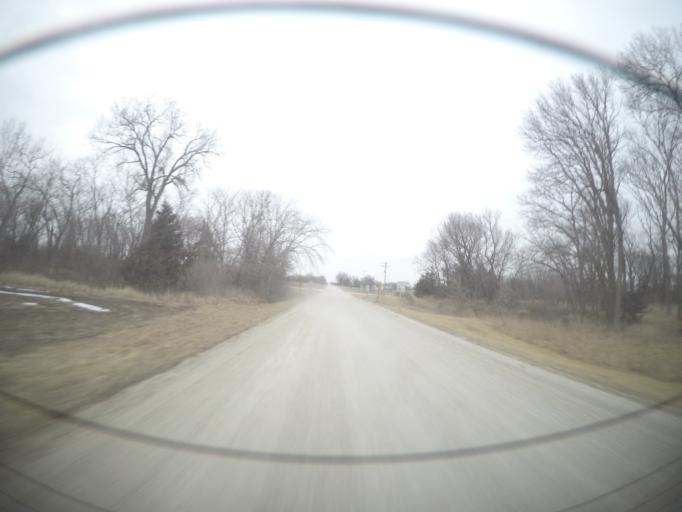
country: US
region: Kansas
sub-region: Pottawatomie County
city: Wamego
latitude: 39.1509
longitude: -96.2407
